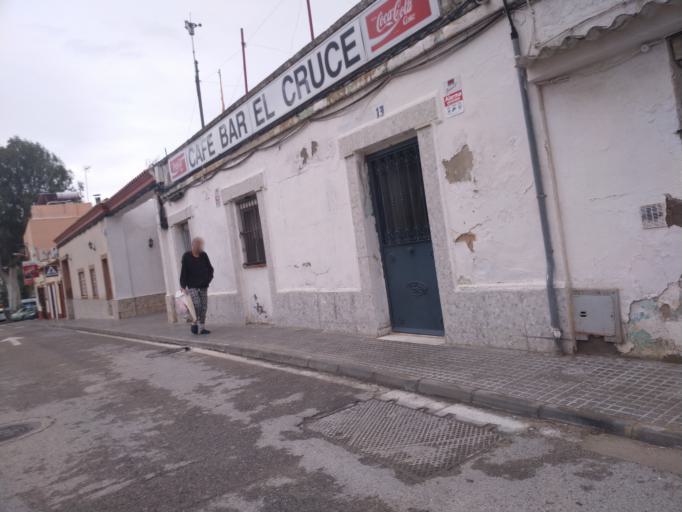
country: ES
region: Andalusia
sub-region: Provincia de Cadiz
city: San Fernando
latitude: 36.4785
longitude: -6.1964
